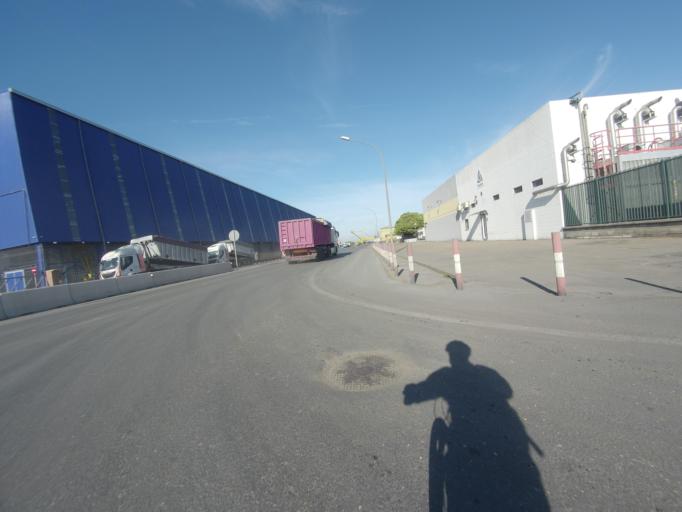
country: ES
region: Andalusia
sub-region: Provincia de Huelva
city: Punta Umbria
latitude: 37.1887
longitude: -6.9284
